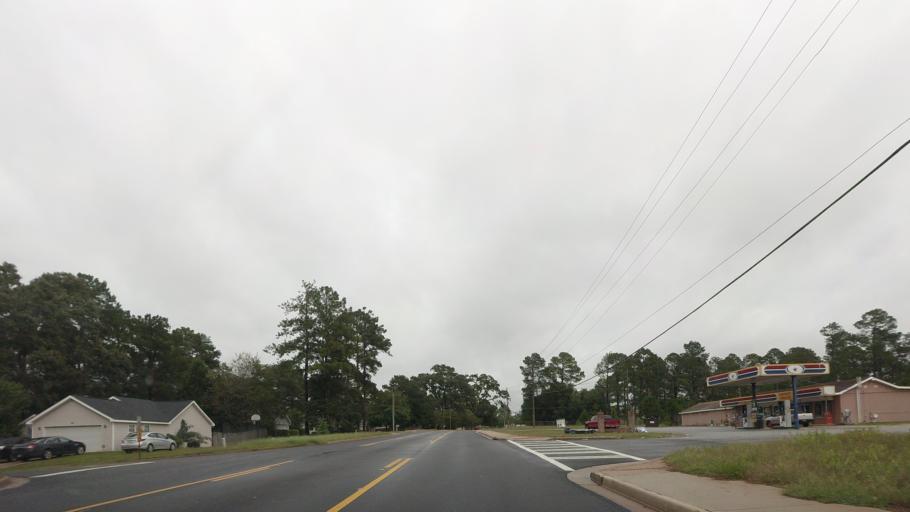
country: US
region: Georgia
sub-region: Houston County
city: Warner Robins
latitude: 32.5739
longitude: -83.6493
